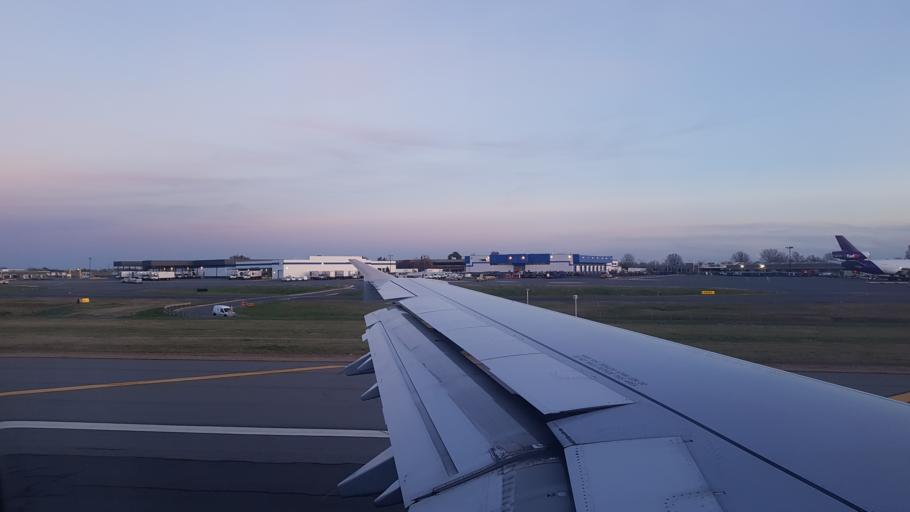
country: US
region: North Carolina
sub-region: Gaston County
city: Belmont
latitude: 35.2145
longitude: -80.9422
